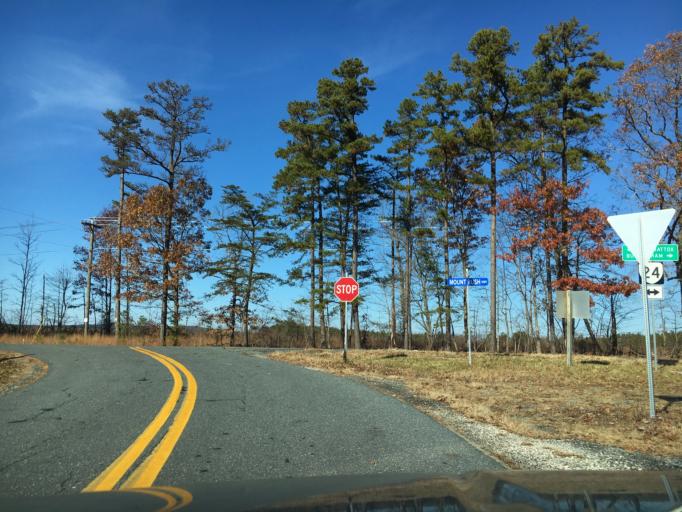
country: US
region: Virginia
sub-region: Buckingham County
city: Buckingham
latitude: 37.4580
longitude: -78.6799
